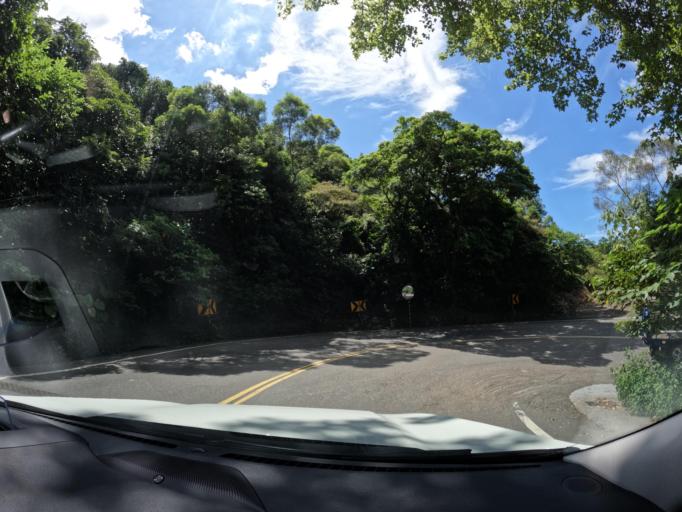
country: TW
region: Taipei
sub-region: Taipei
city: Banqiao
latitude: 25.1153
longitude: 121.3871
